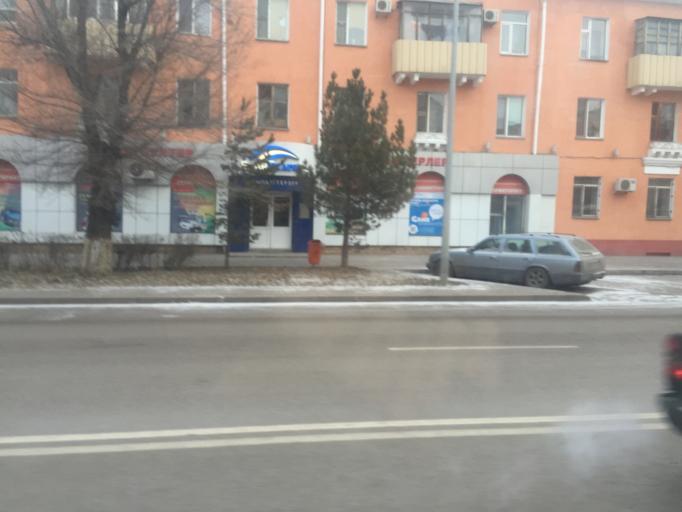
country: KZ
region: Astana Qalasy
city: Astana
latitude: 51.1903
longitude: 71.4104
